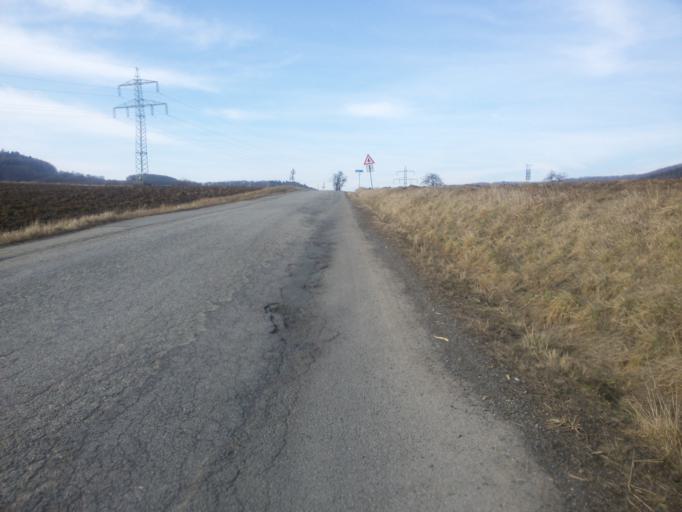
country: CZ
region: South Moravian
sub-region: Okres Brno-Venkov
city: Lomnice
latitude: 49.4188
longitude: 16.3997
